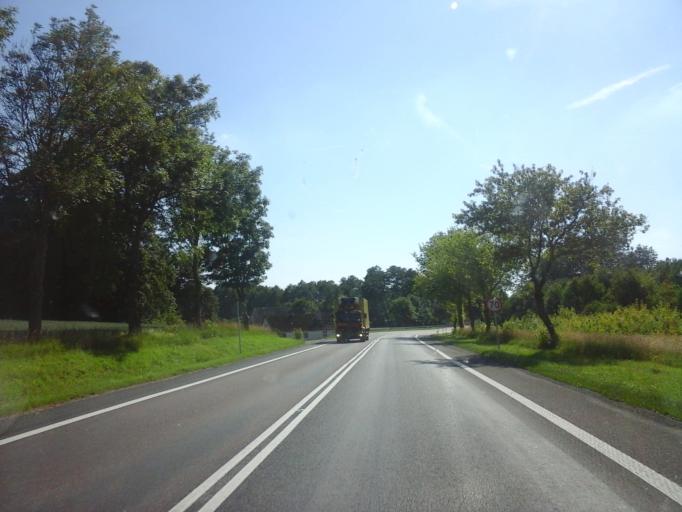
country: PL
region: West Pomeranian Voivodeship
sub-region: Powiat bialogardzki
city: Karlino
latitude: 53.9968
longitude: 15.7729
